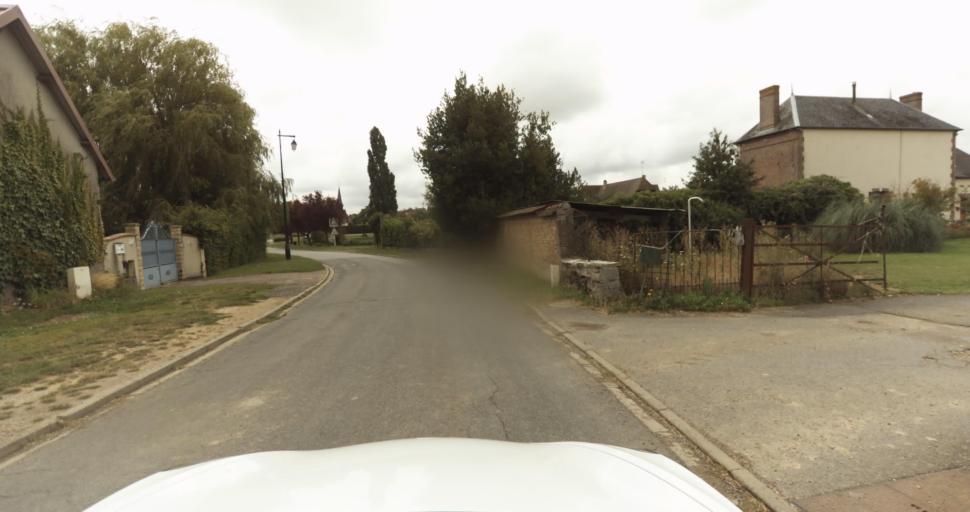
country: FR
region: Haute-Normandie
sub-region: Departement de l'Eure
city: Claville
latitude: 49.0262
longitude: 1.0332
